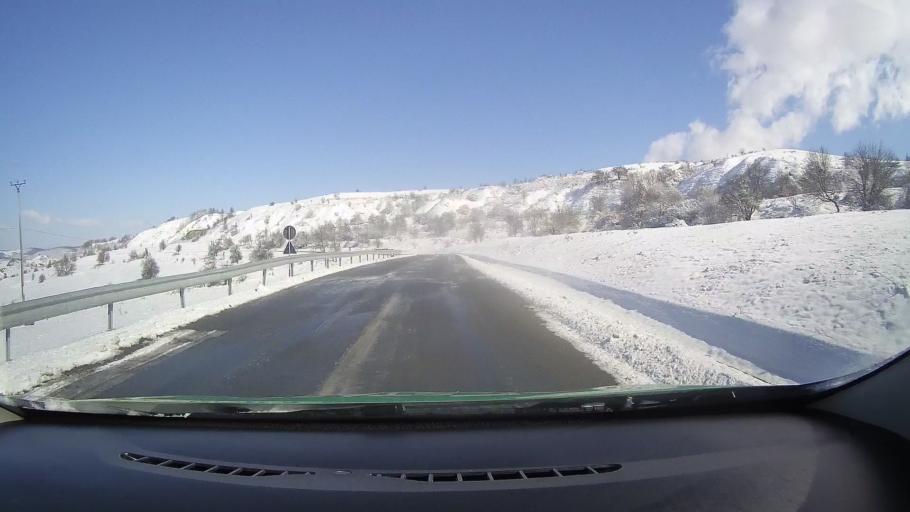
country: RO
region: Sibiu
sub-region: Comuna Avrig
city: Avrig
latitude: 45.7808
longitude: 24.3728
